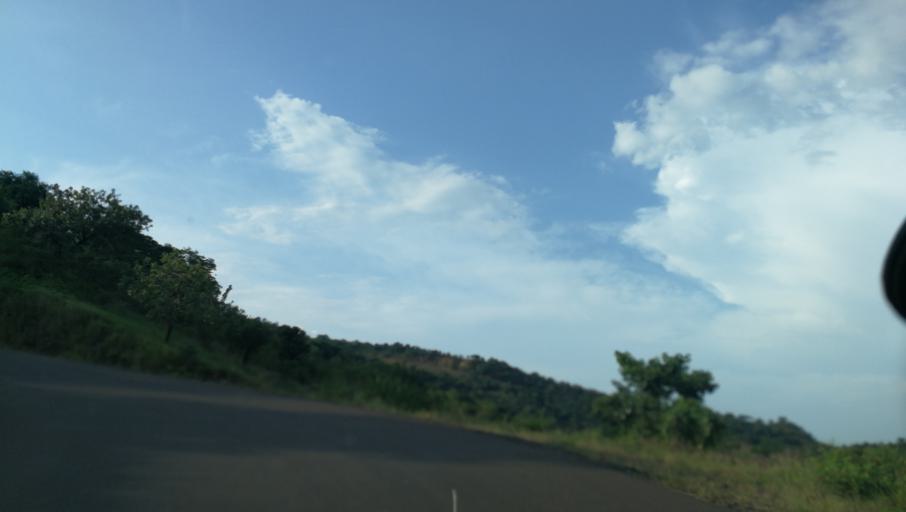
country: ET
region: Southern Nations, Nationalities, and People's Region
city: Areka
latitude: 6.8406
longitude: 37.2763
